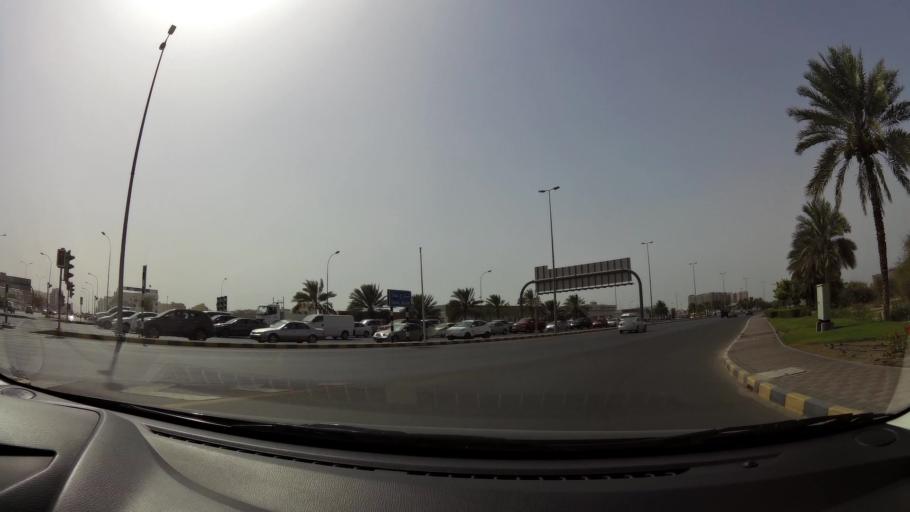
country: OM
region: Muhafazat Masqat
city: Bawshar
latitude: 23.5824
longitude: 58.3816
